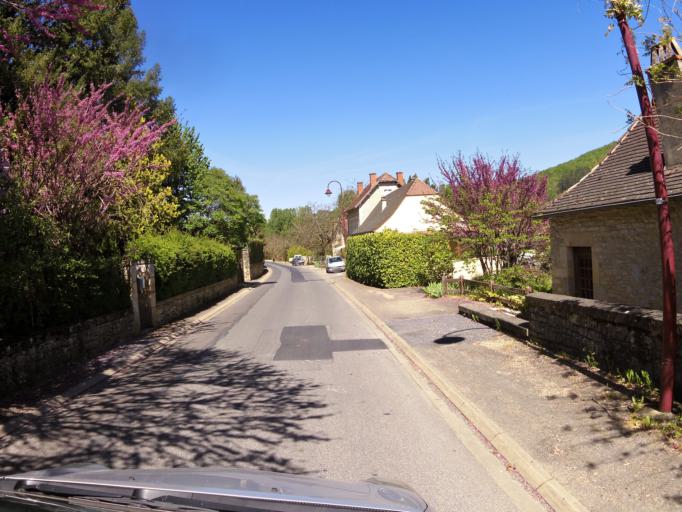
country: FR
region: Aquitaine
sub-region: Departement de la Dordogne
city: Cenac-et-Saint-Julien
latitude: 44.7431
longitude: 1.1905
